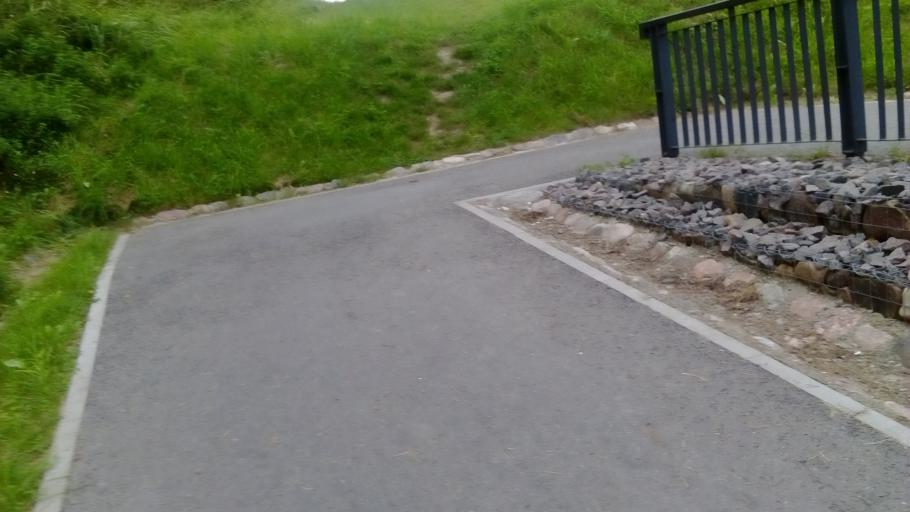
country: LT
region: Alytaus apskritis
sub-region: Alytus
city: Alytus
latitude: 54.4220
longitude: 24.0363
